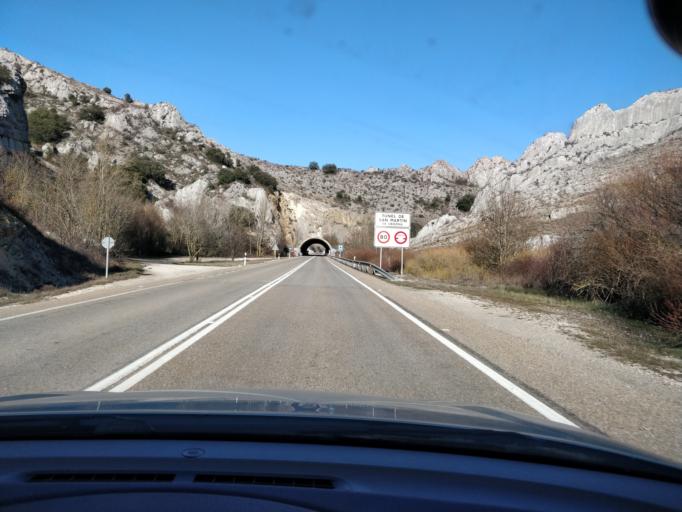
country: ES
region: Castille and Leon
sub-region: Provincia de Burgos
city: Quintanaortuno
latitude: 42.5094
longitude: -3.6970
